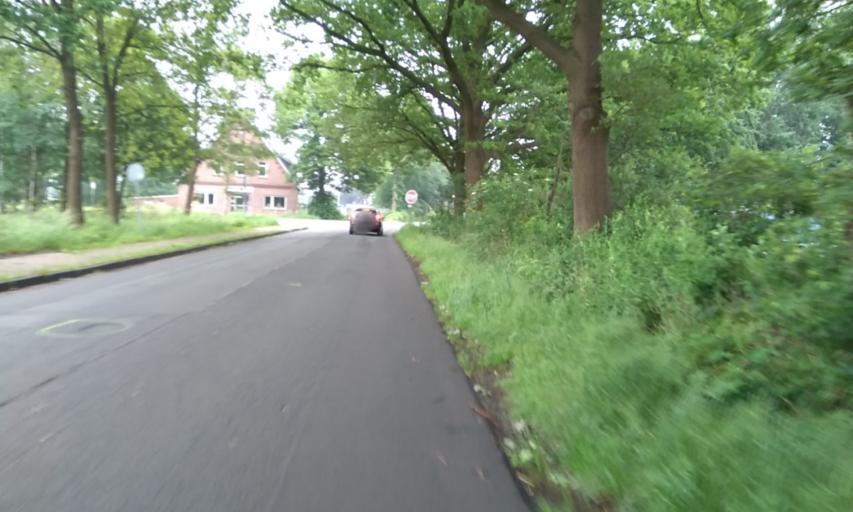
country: DE
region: Lower Saxony
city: Deinste
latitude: 53.5468
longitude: 9.4696
